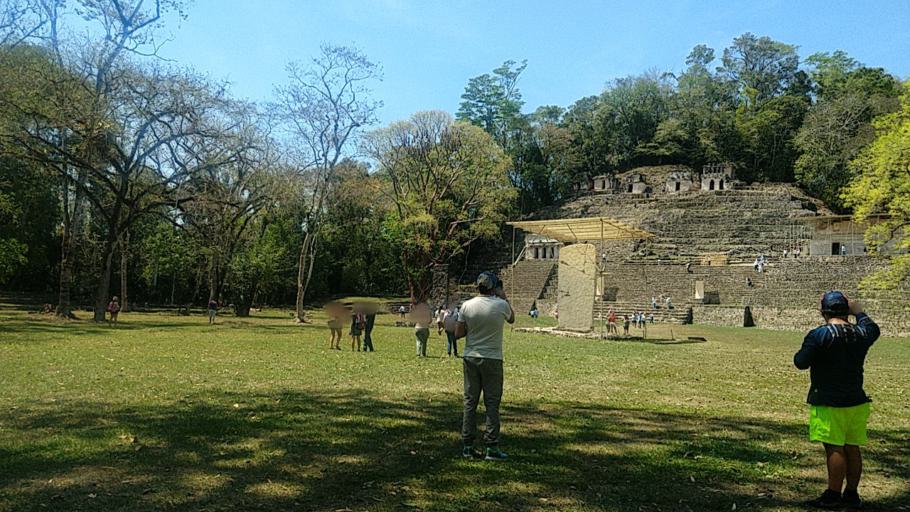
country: MX
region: Chiapas
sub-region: Ocosingo
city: Frontera Corozal
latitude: 16.7045
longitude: -91.0647
